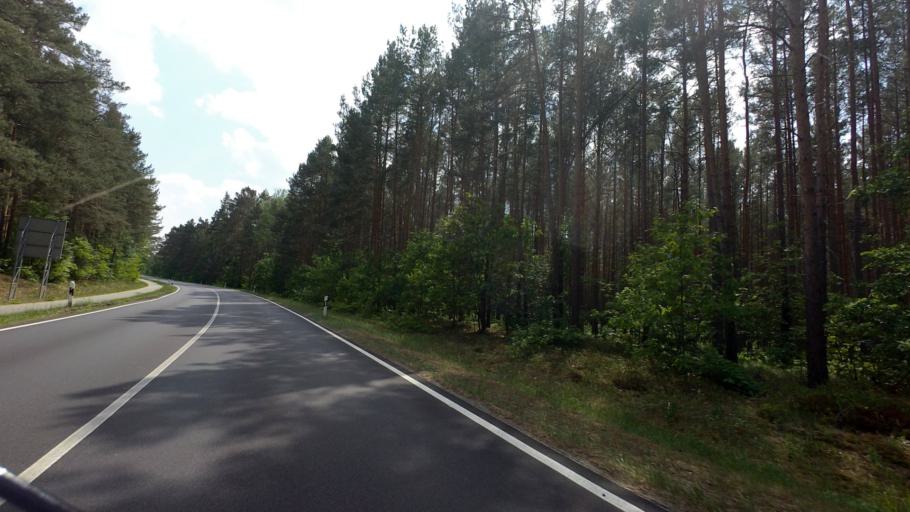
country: DE
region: Saxony
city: Niesky
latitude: 51.3460
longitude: 14.8044
